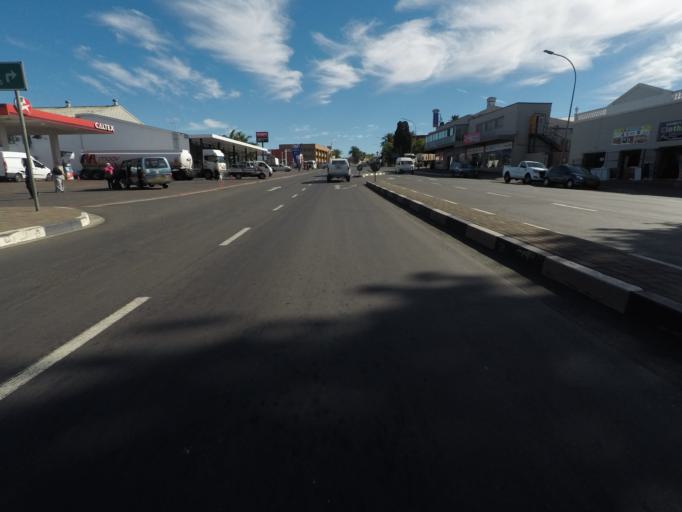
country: ZA
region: Western Cape
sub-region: West Coast District Municipality
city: Malmesbury
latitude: -33.4654
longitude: 18.7290
